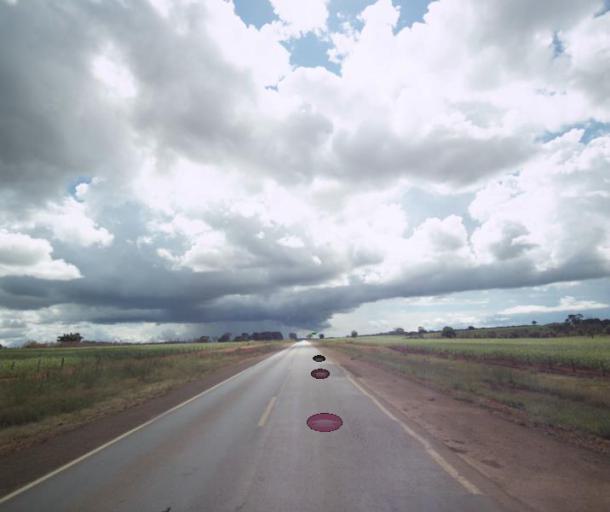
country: BR
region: Goias
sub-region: Uruacu
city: Uruacu
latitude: -14.7012
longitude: -49.1071
